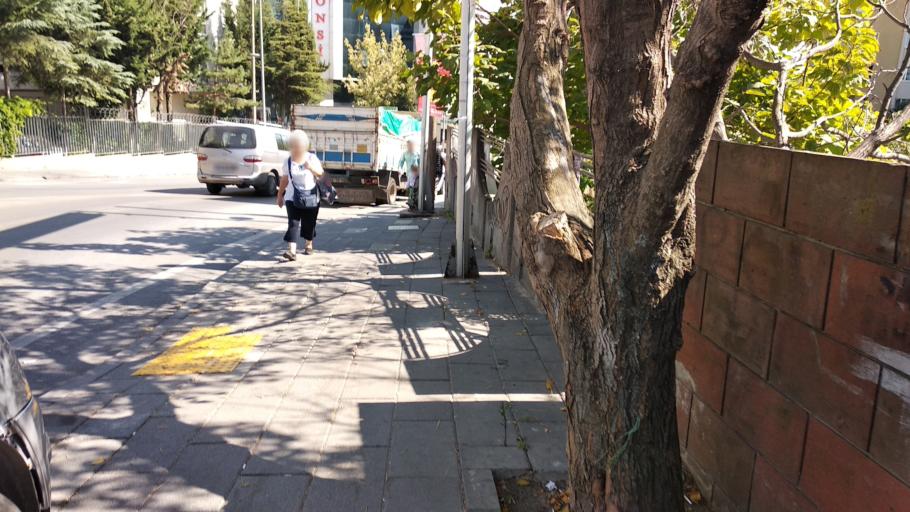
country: TR
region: Istanbul
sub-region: Atasehir
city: Atasehir
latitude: 41.0044
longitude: 29.0727
